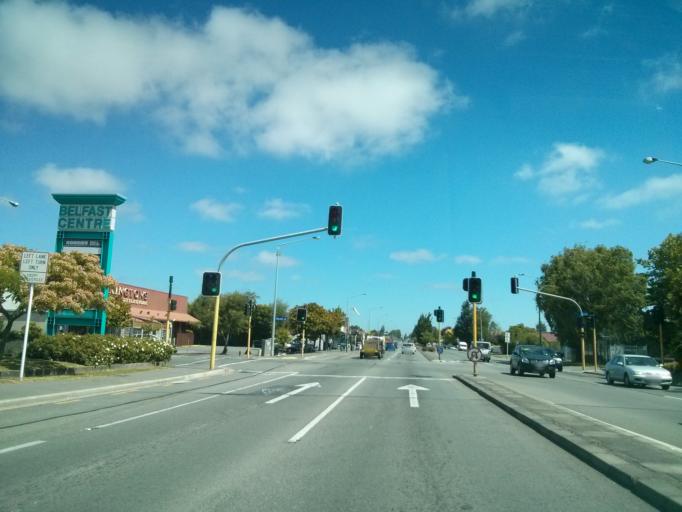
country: NZ
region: Canterbury
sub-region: Waimakariri District
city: Kaiapoi
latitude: -43.4445
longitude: 172.6328
